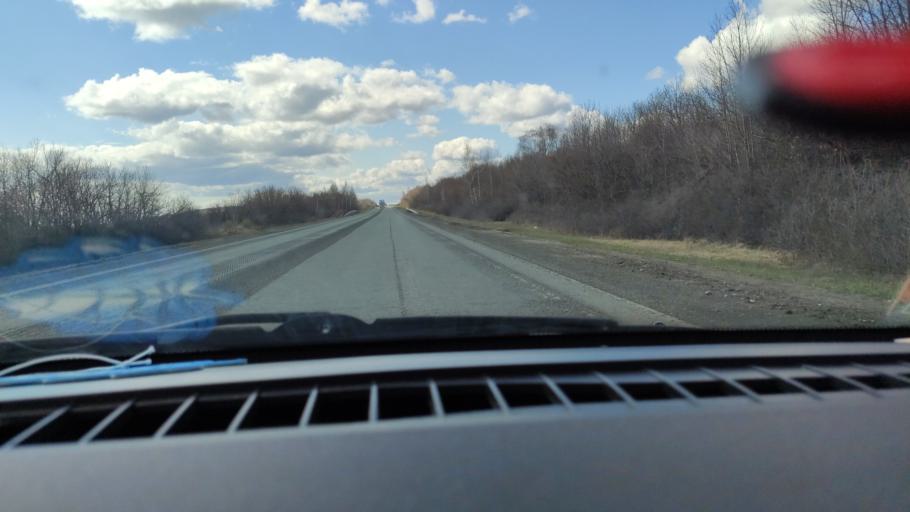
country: RU
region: Saratov
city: Dukhovnitskoye
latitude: 52.6391
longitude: 48.1904
